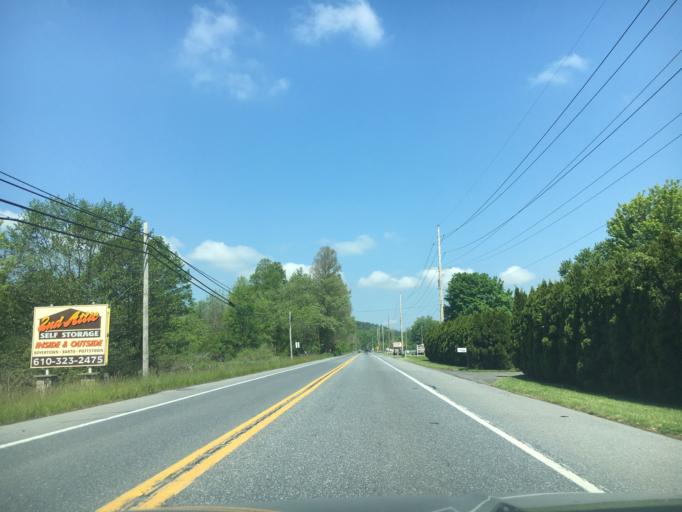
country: US
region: Pennsylvania
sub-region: Berks County
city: Boyertown
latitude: 40.3348
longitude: -75.6524
